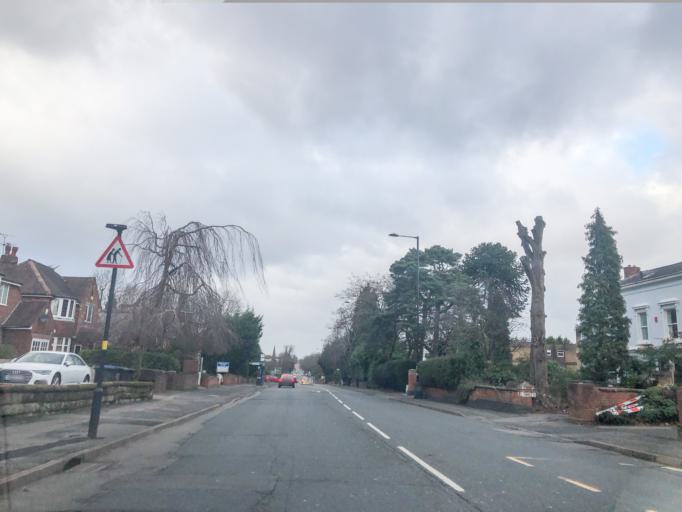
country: GB
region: England
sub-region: Solihull
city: Tidbury Green
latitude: 52.4226
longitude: -1.8922
